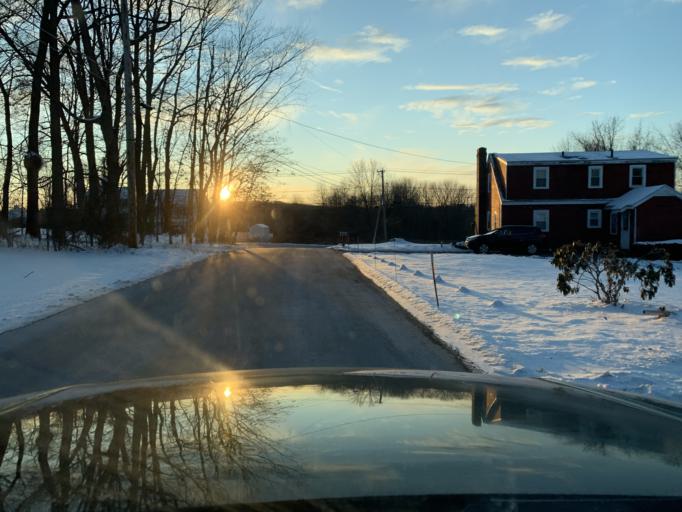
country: US
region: Massachusetts
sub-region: Essex County
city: Haverhill
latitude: 42.7915
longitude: -71.1141
